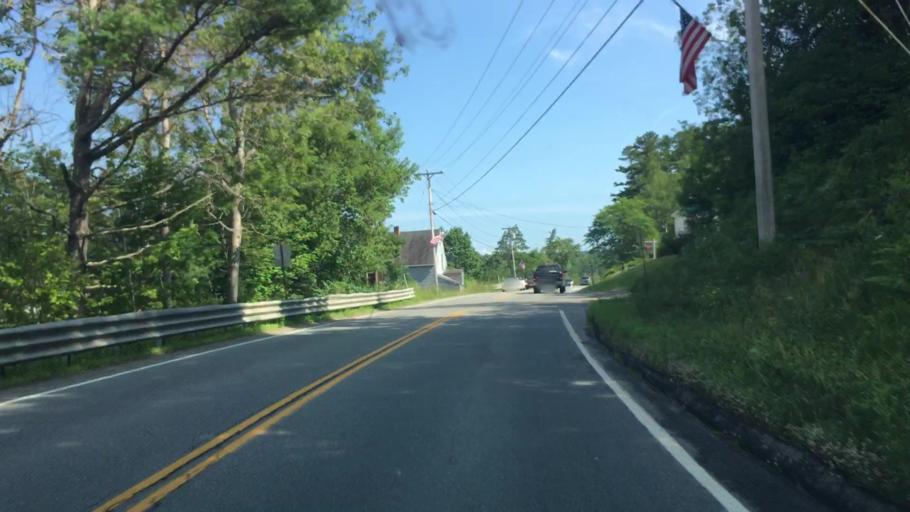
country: US
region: Maine
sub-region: Waldo County
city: Frankfort
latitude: 44.6058
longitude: -68.8723
